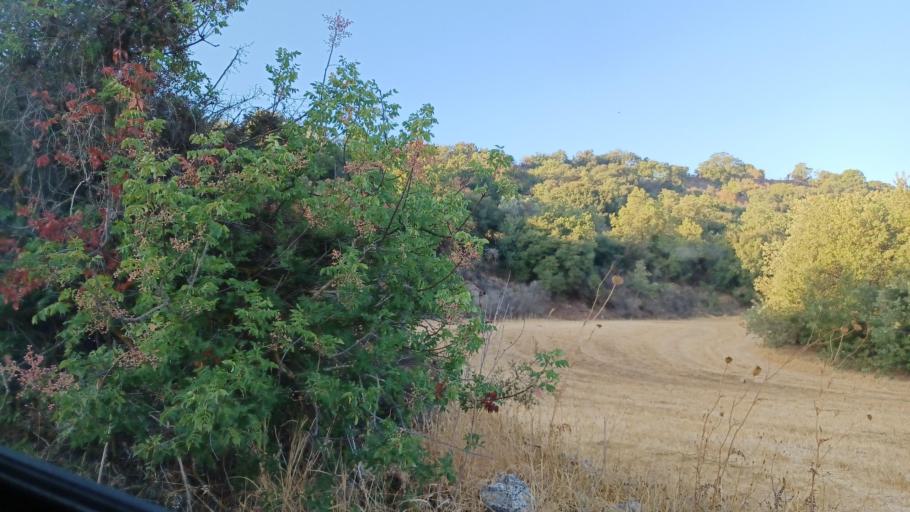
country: CY
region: Pafos
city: Tala
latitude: 34.9241
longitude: 32.4981
